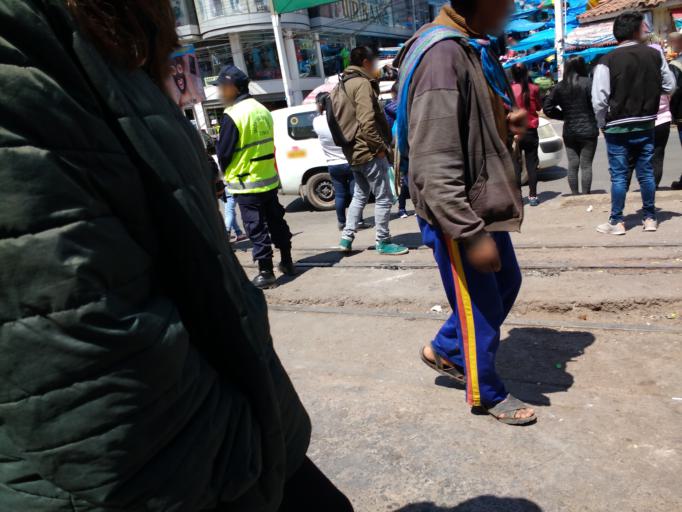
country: PE
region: Cusco
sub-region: Provincia de Cusco
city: Cusco
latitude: -13.5238
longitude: -71.9812
